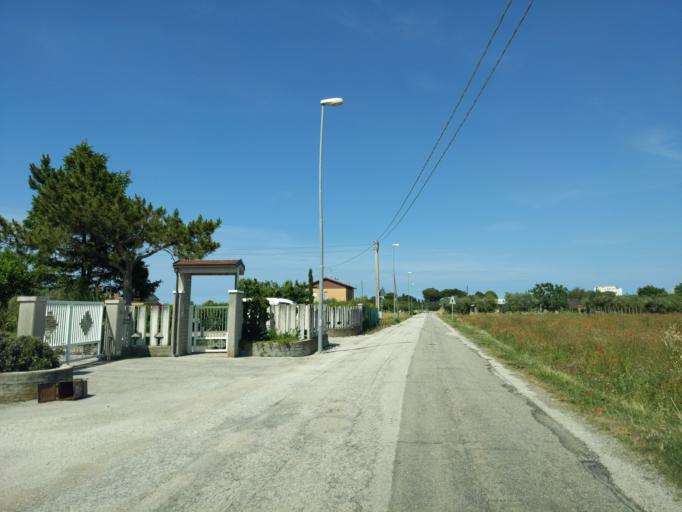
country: IT
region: The Marches
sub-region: Provincia di Pesaro e Urbino
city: Bellocchi
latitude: 43.7994
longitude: 13.0075
